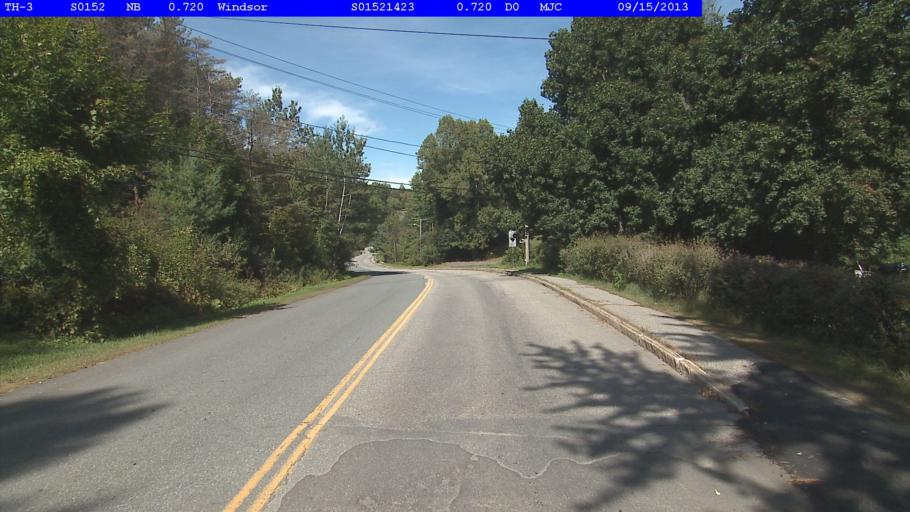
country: US
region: Vermont
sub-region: Windsor County
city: Windsor
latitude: 43.4837
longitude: -72.3994
